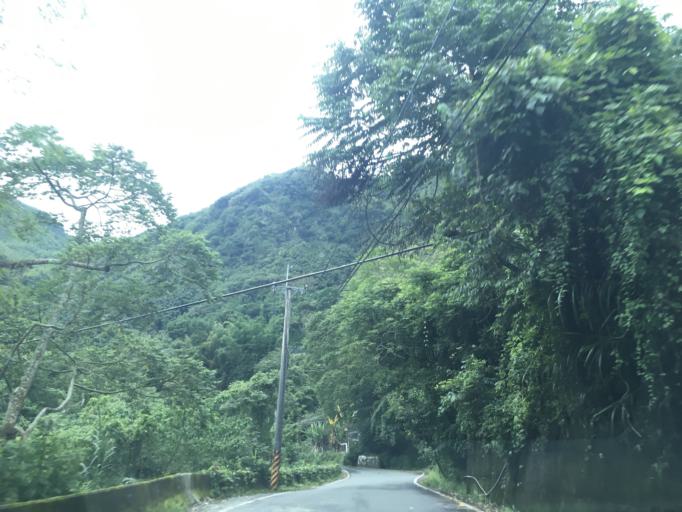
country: TW
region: Taiwan
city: Lugu
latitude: 23.5344
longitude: 120.7011
